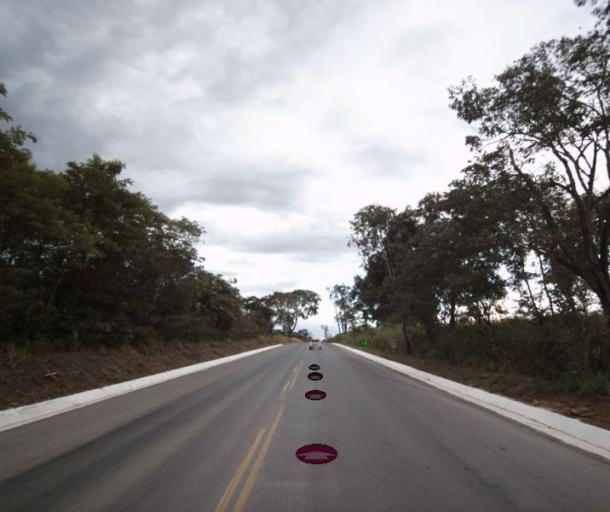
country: BR
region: Goias
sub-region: Itapaci
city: Itapaci
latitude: -14.9844
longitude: -49.4002
